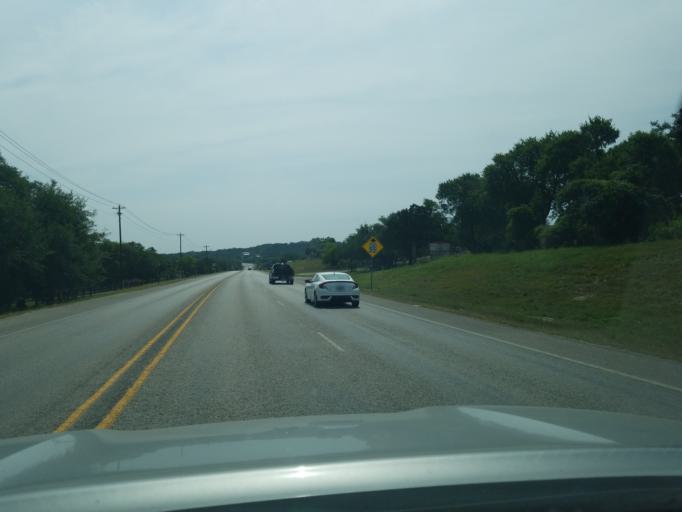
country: US
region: Texas
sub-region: Comal County
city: Bulverde
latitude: 29.7970
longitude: -98.4538
